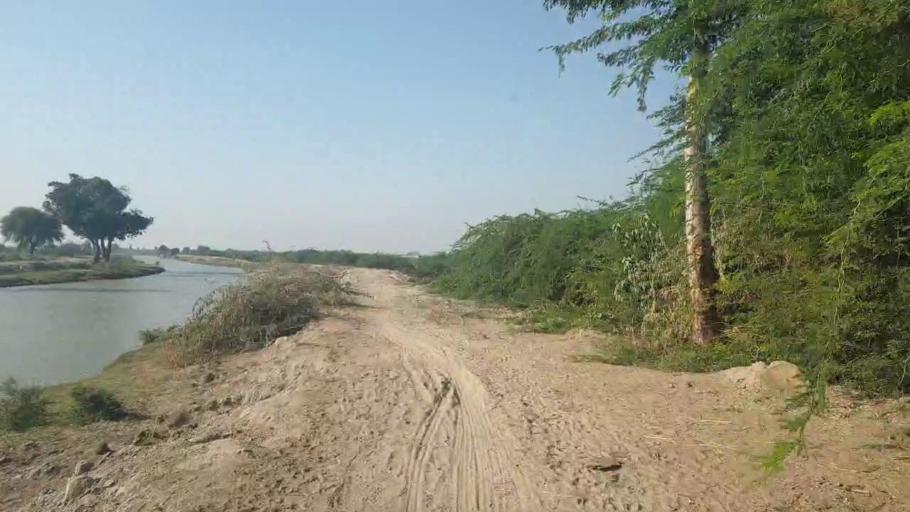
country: PK
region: Sindh
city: Badin
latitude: 24.6944
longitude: 68.8713
